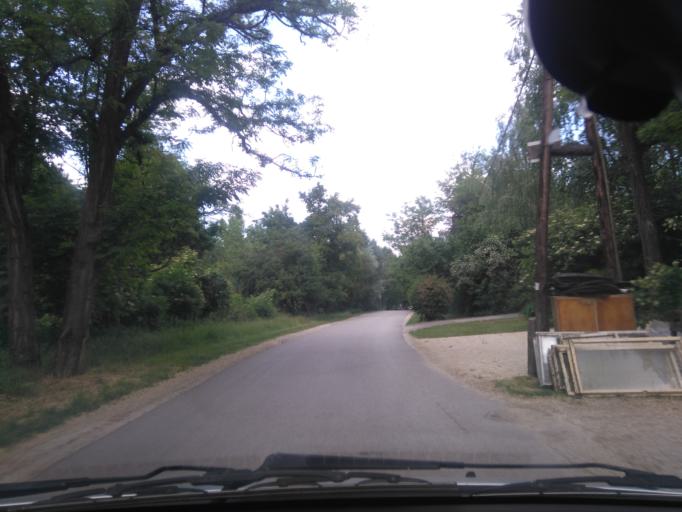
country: HU
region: Pest
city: Szob
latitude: 47.8117
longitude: 18.8119
